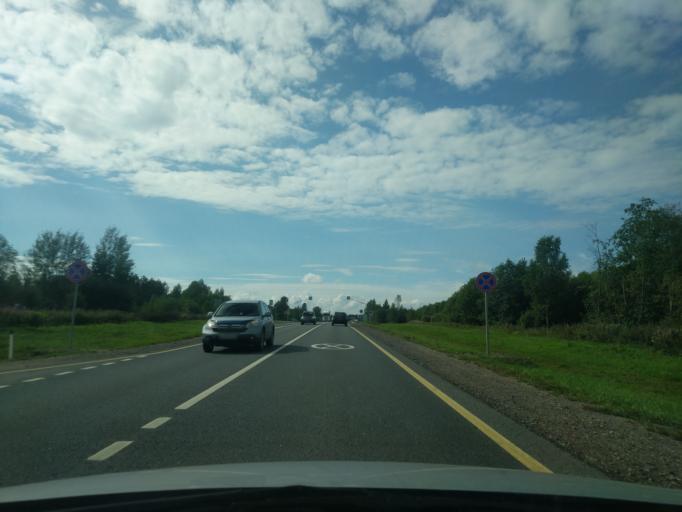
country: RU
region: Kostroma
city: Oktyabr'skiy
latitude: 57.7980
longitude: 41.2276
